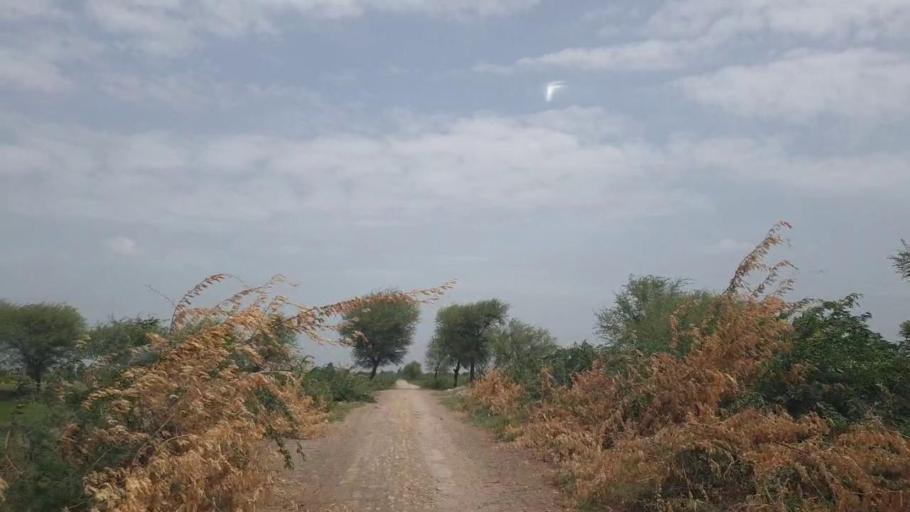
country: PK
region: Sindh
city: Tando Bago
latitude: 24.9256
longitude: 69.0999
